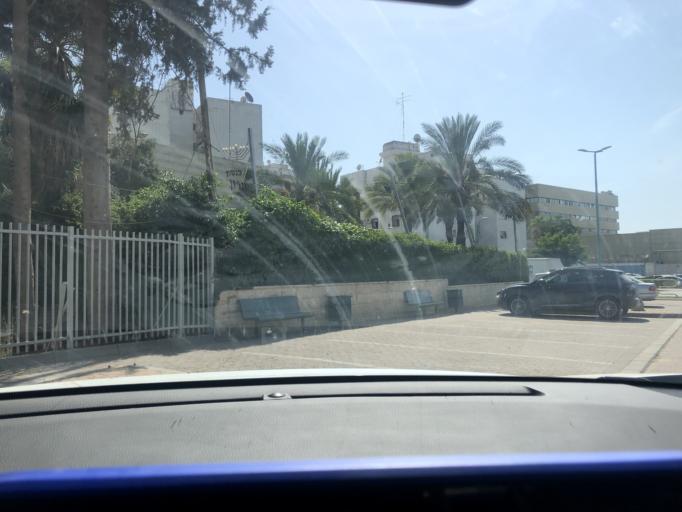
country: IL
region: Central District
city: Lod
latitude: 31.9523
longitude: 34.8927
